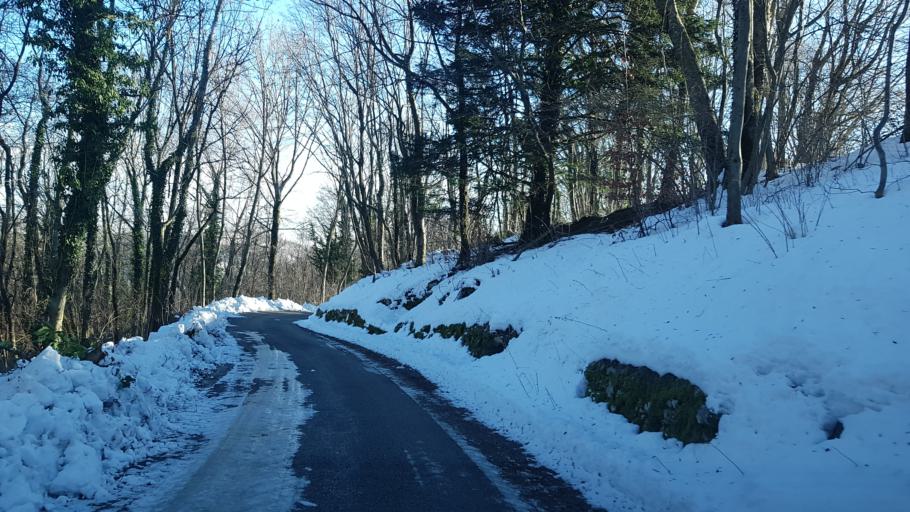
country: IT
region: Friuli Venezia Giulia
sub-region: Provincia di Udine
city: Forgaria nel Friuli
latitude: 46.2591
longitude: 12.9931
